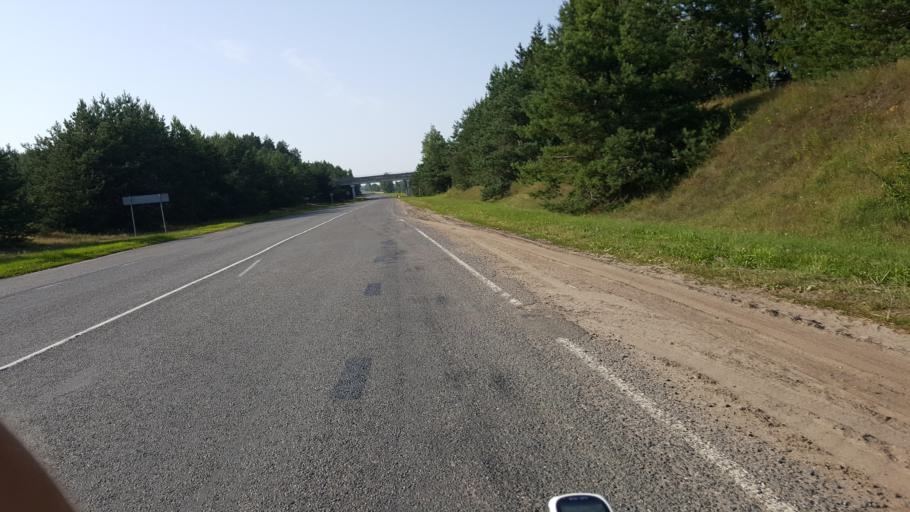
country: BY
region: Brest
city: Kamyanyets
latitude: 52.3403
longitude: 23.9078
